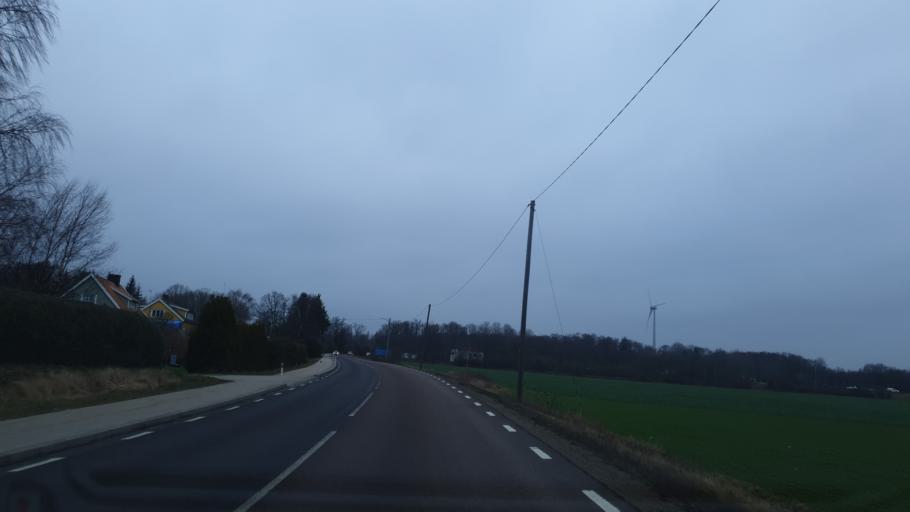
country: SE
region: Blekinge
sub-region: Karlskrona Kommun
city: Jaemjoe
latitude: 56.1804
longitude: 15.7211
